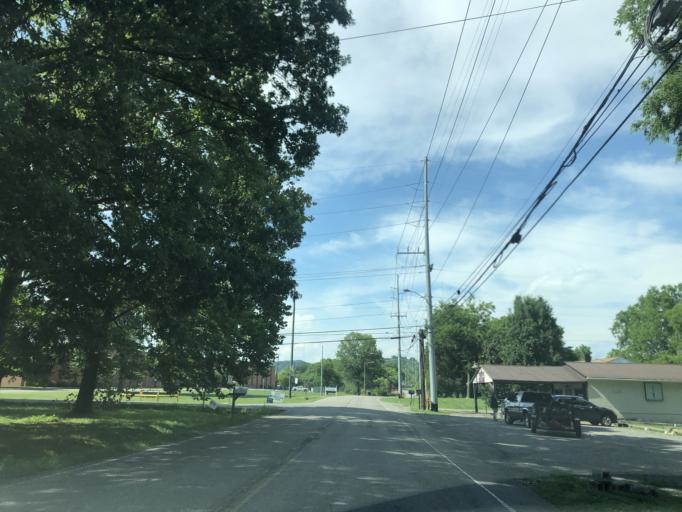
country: US
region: Tennessee
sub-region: Davidson County
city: Nashville
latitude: 36.2363
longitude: -86.8032
